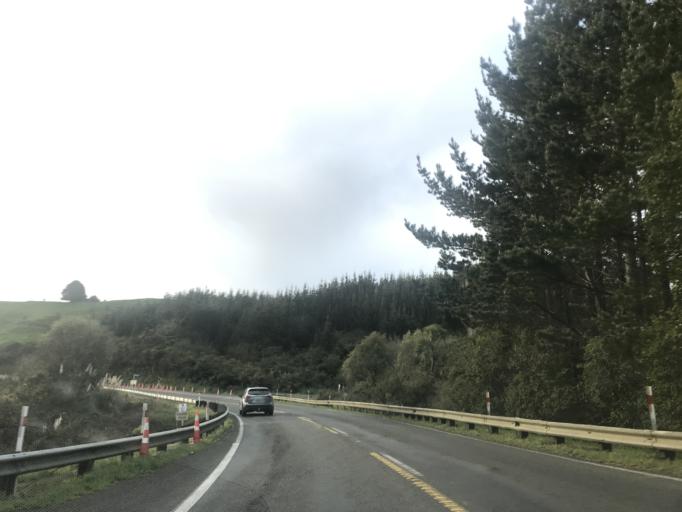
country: NZ
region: Bay of Plenty
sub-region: Western Bay of Plenty District
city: Waihi Beach
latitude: -37.4534
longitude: 175.8927
